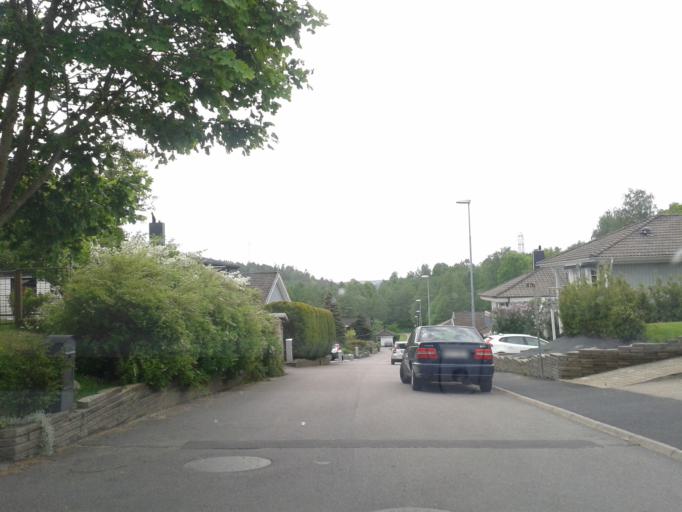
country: SE
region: Vaestra Goetaland
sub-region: Kungalvs Kommun
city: Kungalv
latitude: 57.8832
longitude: 11.9583
